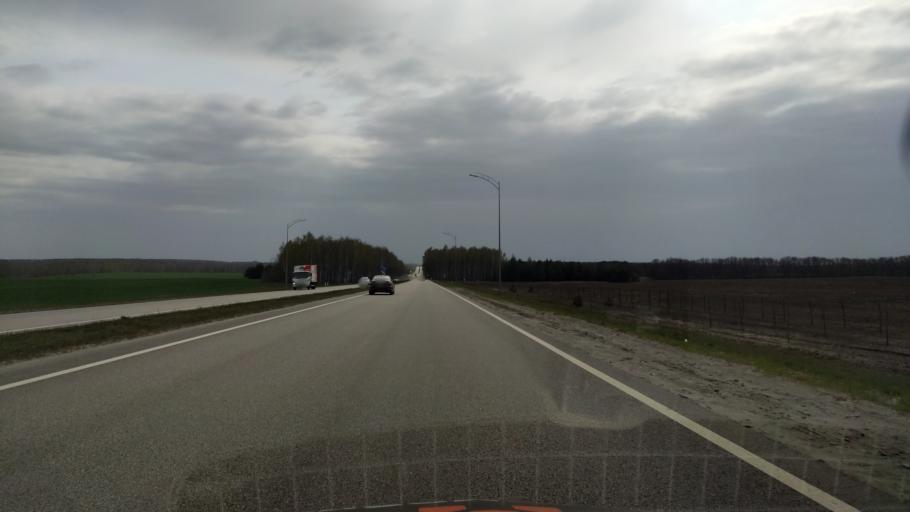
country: RU
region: Belgorod
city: Staryy Oskol
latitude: 51.4151
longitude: 37.8868
